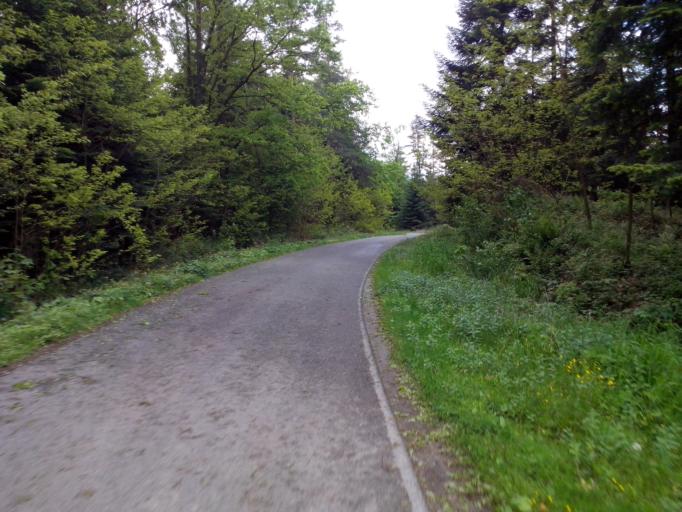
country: PL
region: Subcarpathian Voivodeship
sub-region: Powiat strzyzowski
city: Wysoka Strzyzowska
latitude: 49.8252
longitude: 21.7824
